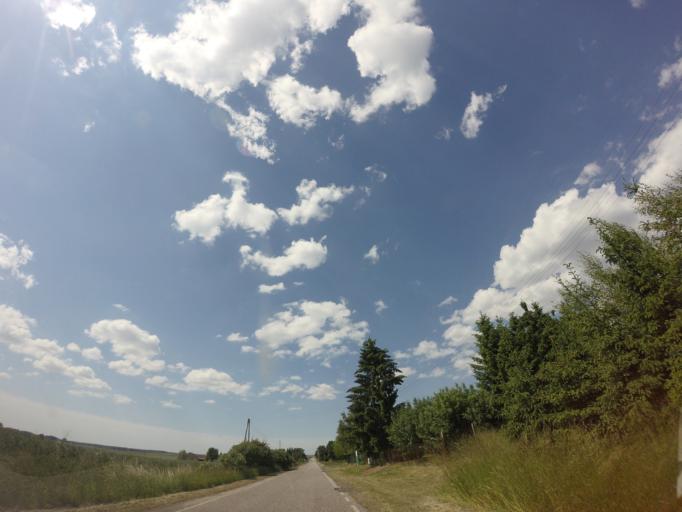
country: PL
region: West Pomeranian Voivodeship
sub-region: Powiat stargardzki
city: Dolice
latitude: 53.1619
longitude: 15.2325
